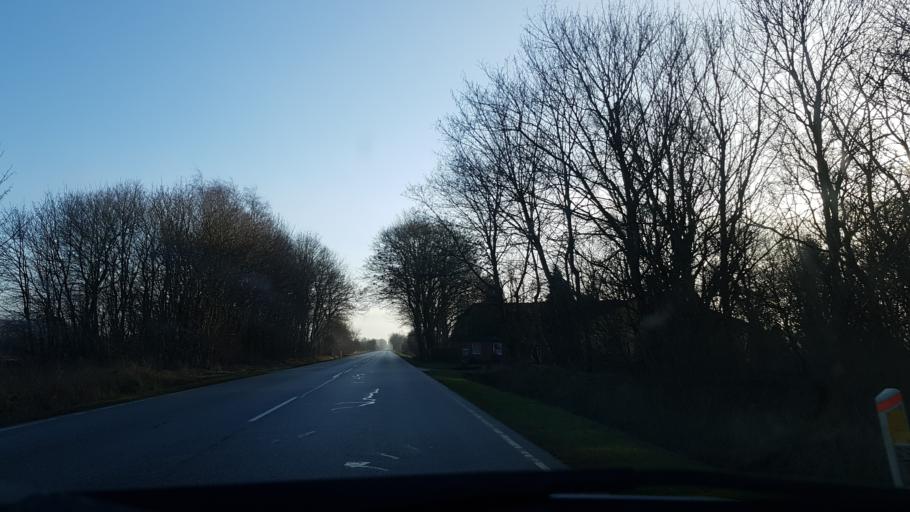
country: DK
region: South Denmark
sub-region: Tonder Kommune
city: Toftlund
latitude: 55.2354
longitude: 9.1645
